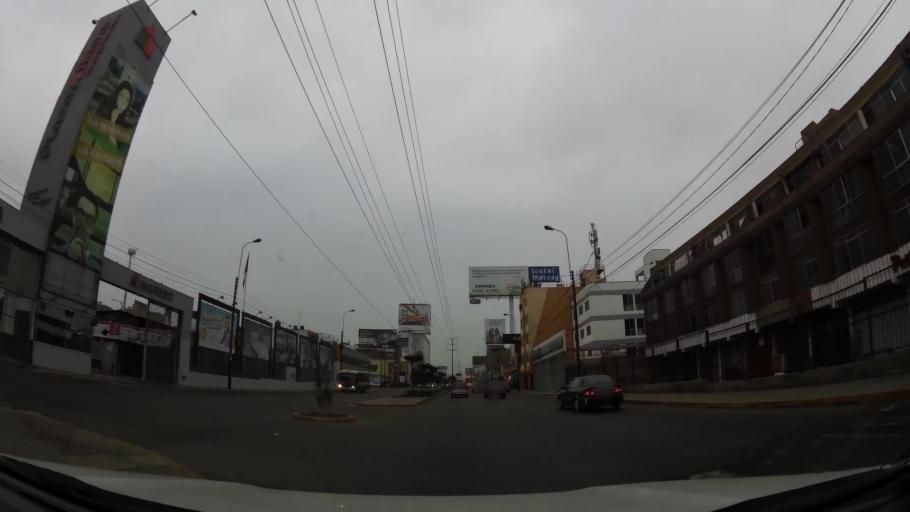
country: PE
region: Lima
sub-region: Lima
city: Surco
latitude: -12.1127
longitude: -77.0146
